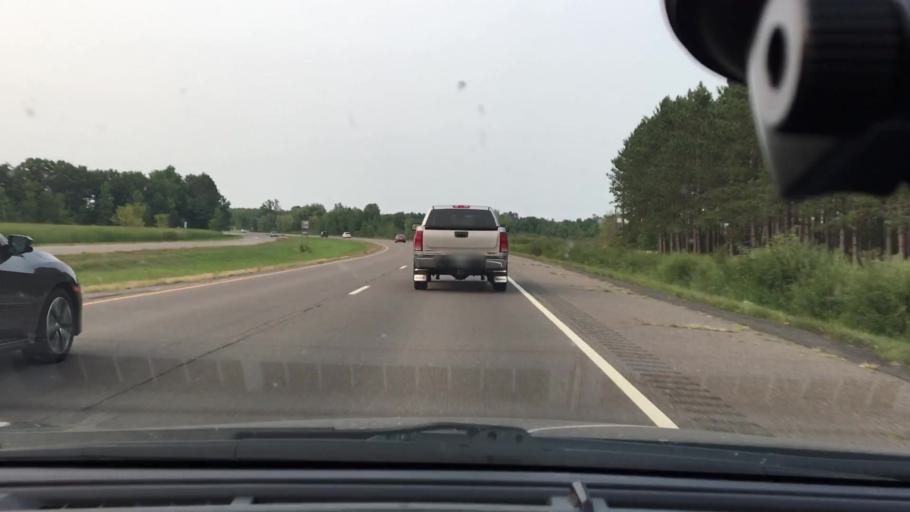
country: US
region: Minnesota
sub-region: Mille Lacs County
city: Vineland
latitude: 46.0900
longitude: -93.6450
